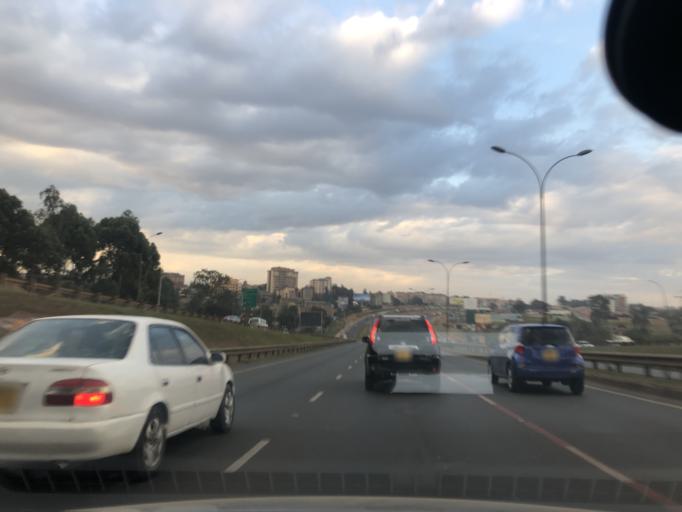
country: KE
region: Nairobi Area
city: Pumwani
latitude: -1.2414
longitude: 36.8693
